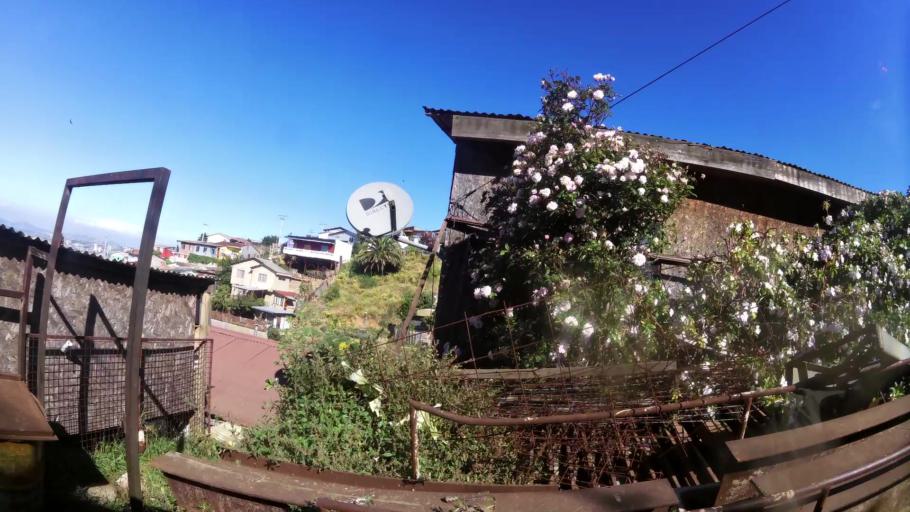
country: CL
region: Valparaiso
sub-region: Provincia de Valparaiso
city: Valparaiso
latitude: -33.0608
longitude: -71.6211
